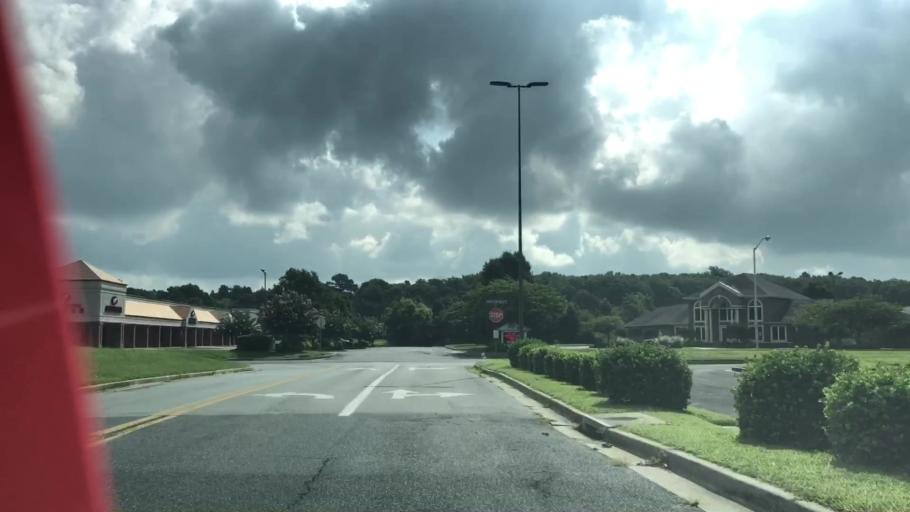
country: US
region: Maryland
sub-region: Wicomico County
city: Salisbury
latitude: 38.4011
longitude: -75.5633
